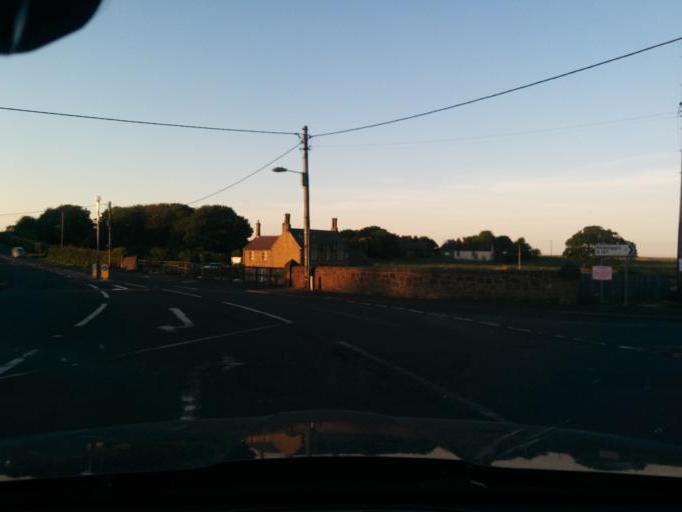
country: GB
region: England
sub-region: Northumberland
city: Newbiggin-by-the-Sea
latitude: 55.1935
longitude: -1.5333
